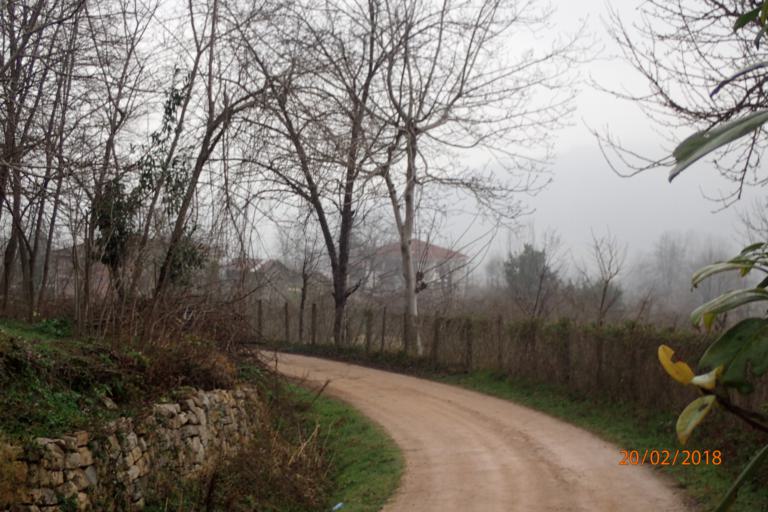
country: TR
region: Ordu
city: Camas
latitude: 40.9467
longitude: 37.5227
